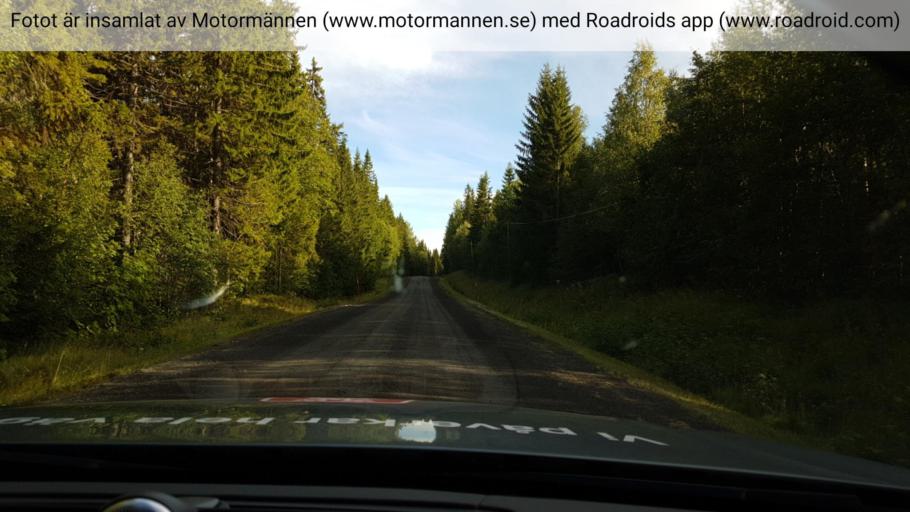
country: SE
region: Jaemtland
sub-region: Stroemsunds Kommun
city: Stroemsund
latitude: 64.1037
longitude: 15.8216
